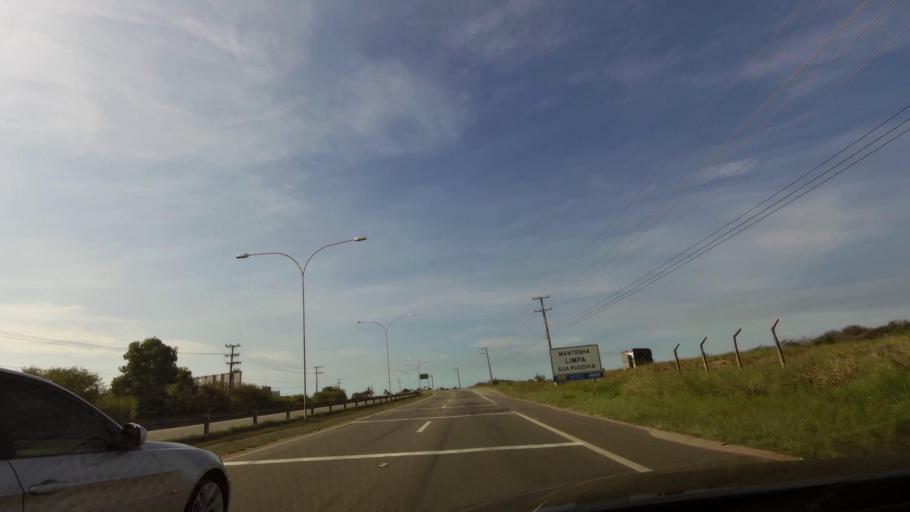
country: BR
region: Espirito Santo
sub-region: Vila Velha
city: Vila Velha
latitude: -20.4524
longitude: -40.3360
